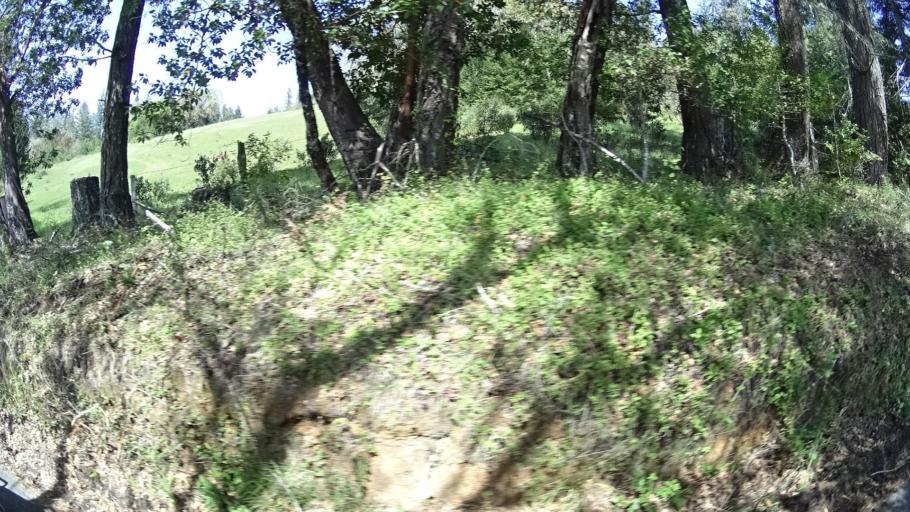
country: US
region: California
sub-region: Humboldt County
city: Redway
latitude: 40.2793
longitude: -123.6416
